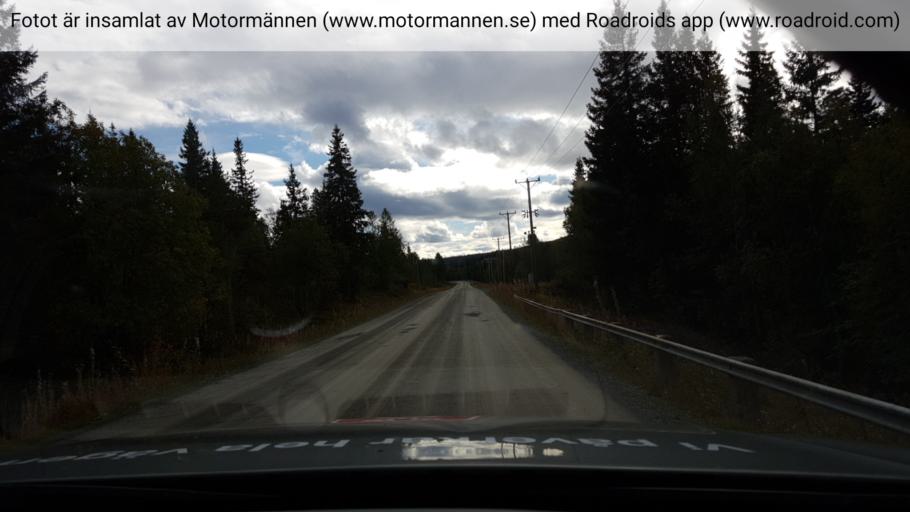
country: SE
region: Jaemtland
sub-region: Are Kommun
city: Are
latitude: 63.6832
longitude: 12.8088
